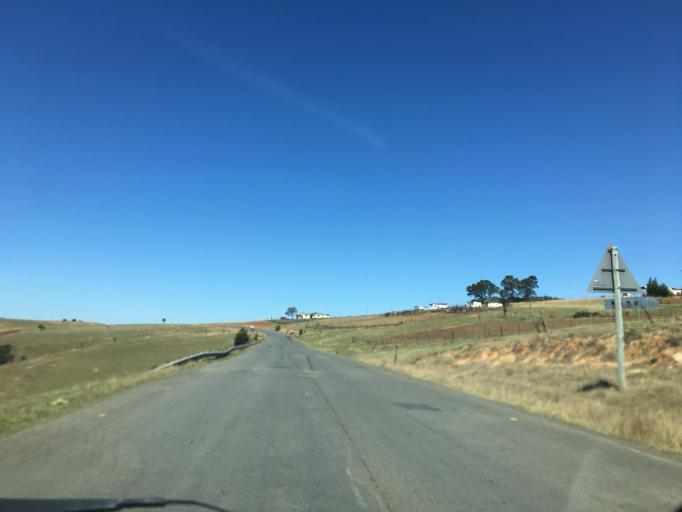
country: ZA
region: Eastern Cape
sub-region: Chris Hani District Municipality
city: Cala
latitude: -31.5590
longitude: 27.8974
